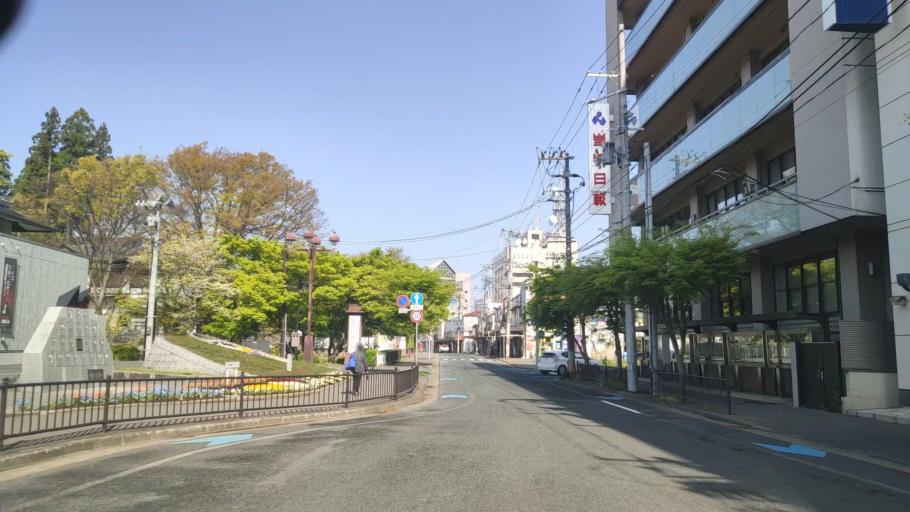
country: JP
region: Iwate
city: Morioka-shi
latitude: 39.7013
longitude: 141.1532
